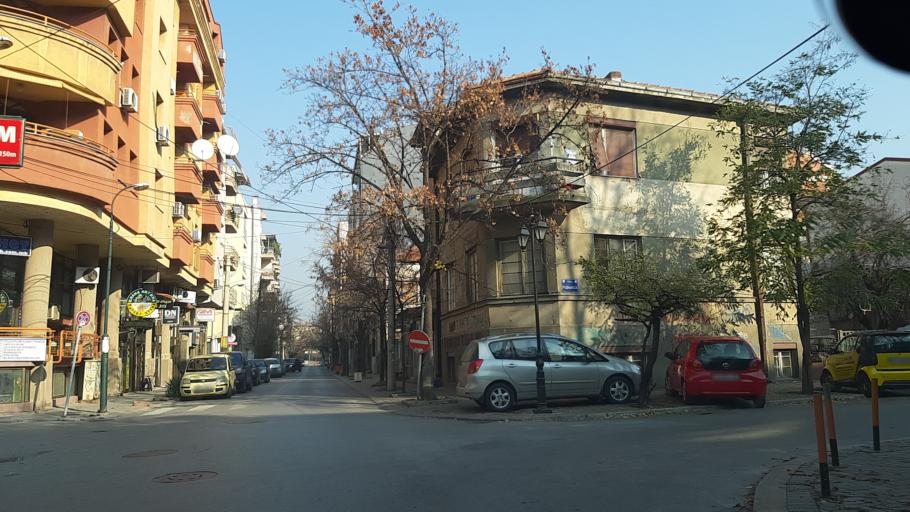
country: MK
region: Karpos
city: Skopje
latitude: 42.0007
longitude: 21.4181
